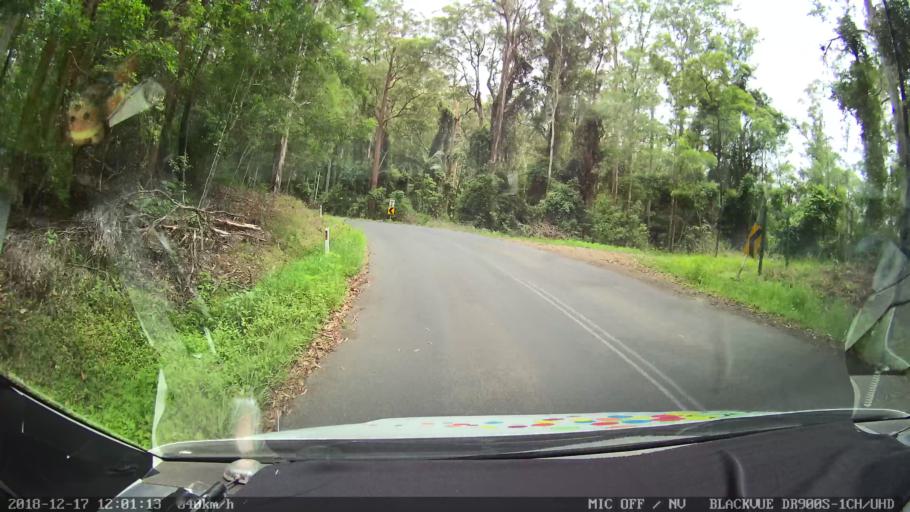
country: AU
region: New South Wales
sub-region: Kyogle
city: Kyogle
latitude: -28.5228
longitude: 152.5723
